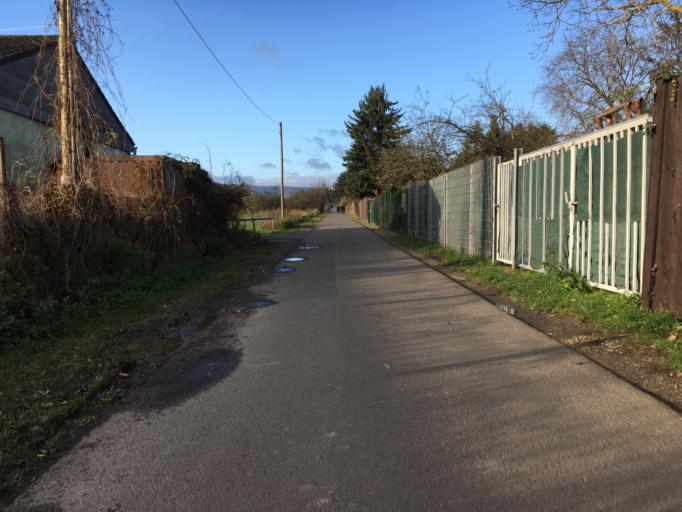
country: DE
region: Hesse
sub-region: Regierungsbezirk Darmstadt
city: Wiesbaden
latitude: 50.0541
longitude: 8.2356
